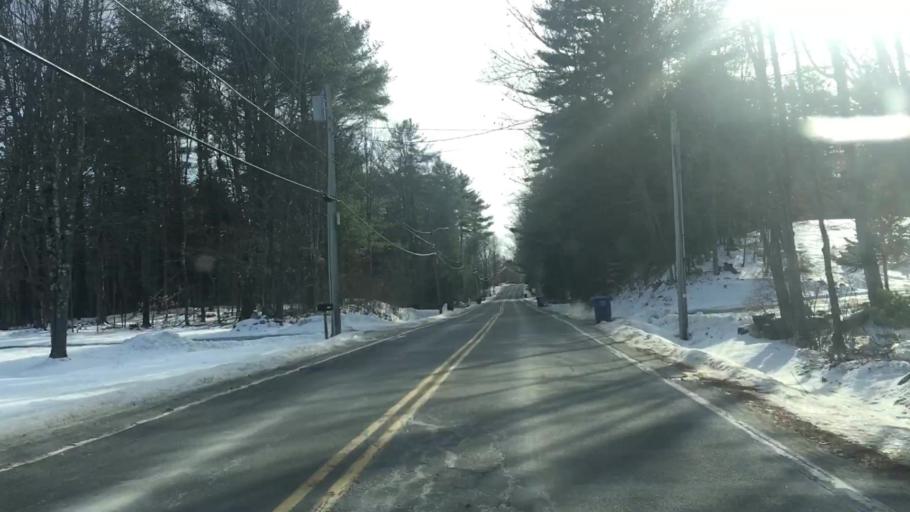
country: US
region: Maine
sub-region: Cumberland County
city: Westbrook
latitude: 43.7248
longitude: -70.3572
